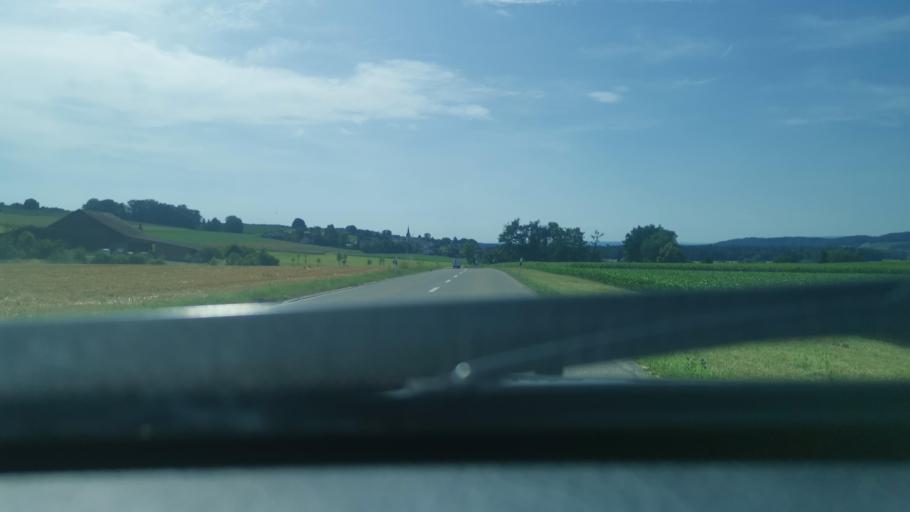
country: CH
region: Zurich
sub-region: Bezirk Winterthur
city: Sulz
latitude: 47.5705
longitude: 8.7933
